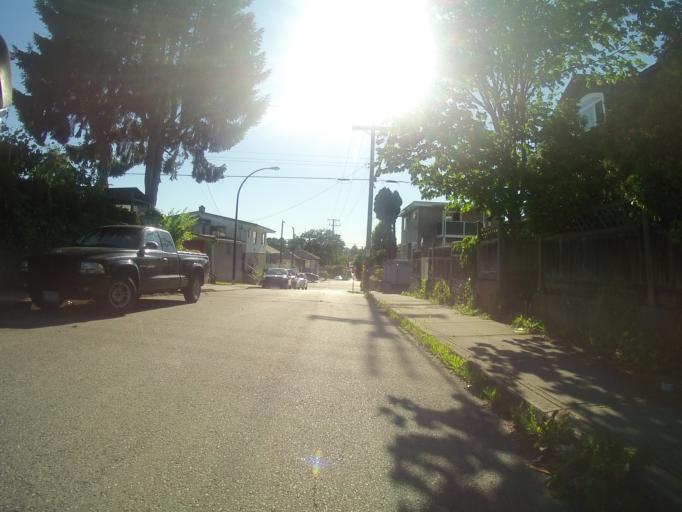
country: CA
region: British Columbia
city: Vancouver
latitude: 49.2428
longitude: -123.0643
